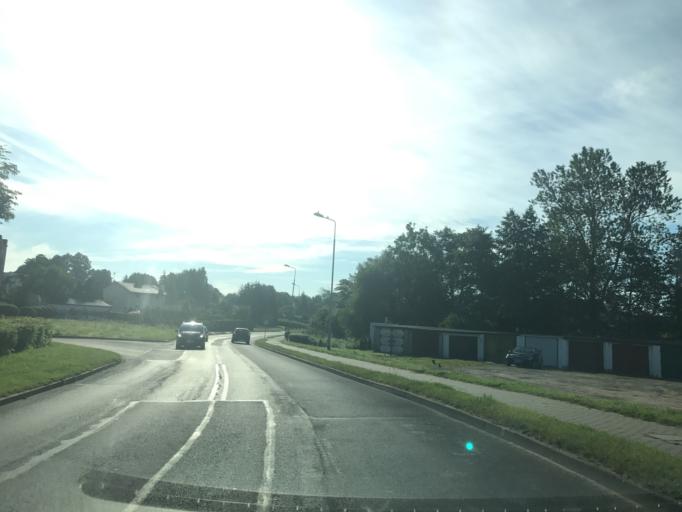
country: PL
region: West Pomeranian Voivodeship
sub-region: Powiat koszalinski
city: Bobolice
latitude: 53.9513
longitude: 16.5907
